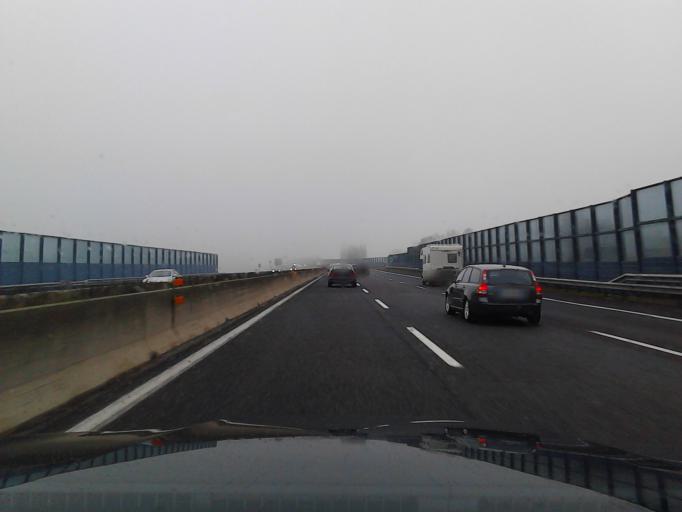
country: IT
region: Emilia-Romagna
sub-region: Forli-Cesena
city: Santa Maria Nuova
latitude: 44.2106
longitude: 12.1878
